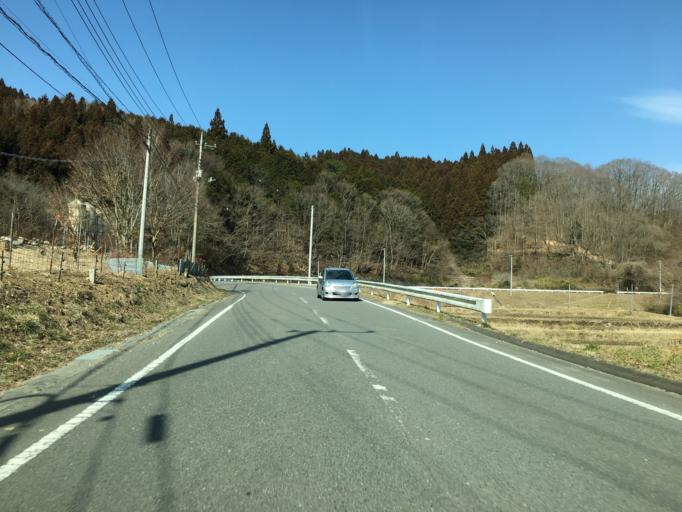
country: JP
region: Ibaraki
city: Daigo
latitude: 36.8161
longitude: 140.5151
